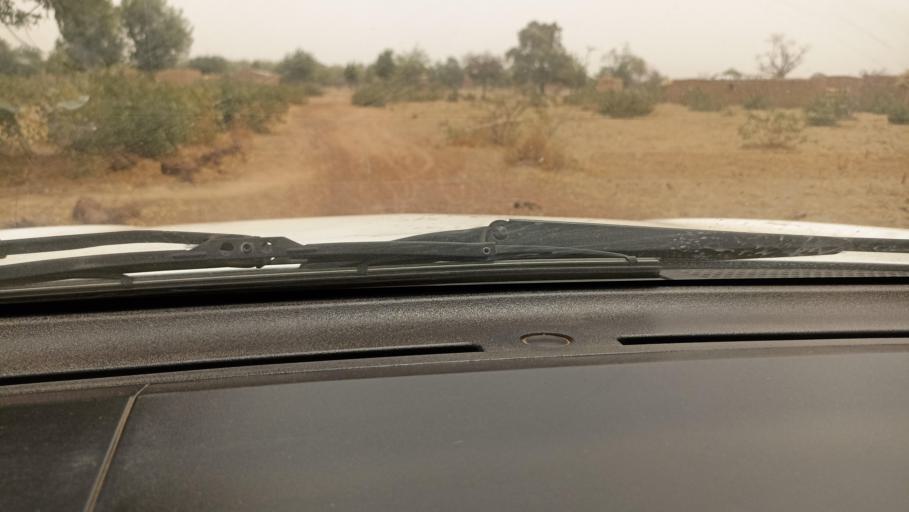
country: BF
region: Boucle du Mouhoun
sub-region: Province du Nayala
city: Toma
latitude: 12.8667
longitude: -2.7487
